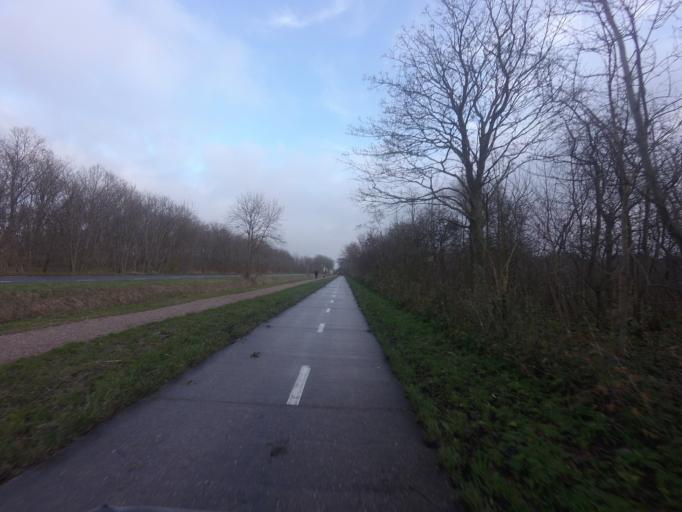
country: NL
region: North Holland
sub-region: Gemeente Texel
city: Den Burg
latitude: 53.1568
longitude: 4.8593
